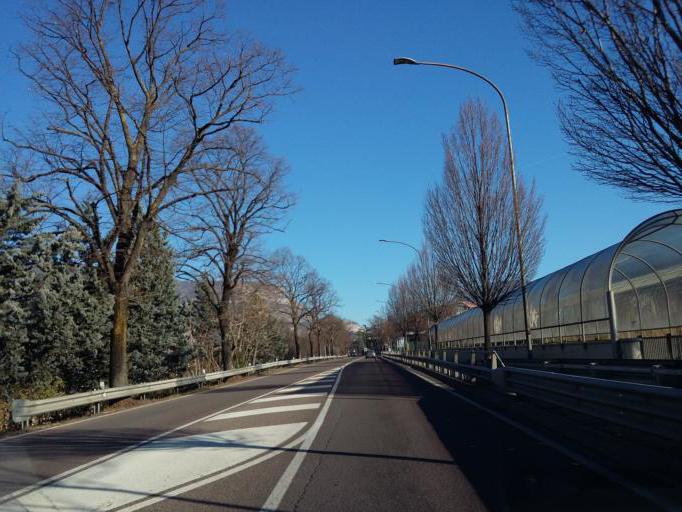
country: IT
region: Trentino-Alto Adige
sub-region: Provincia di Trento
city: Villa Lagarina
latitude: 45.9052
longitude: 11.0377
